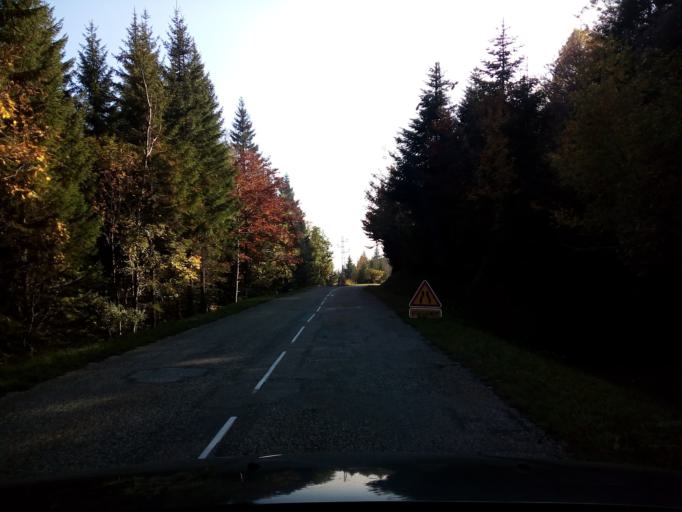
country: FR
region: Rhone-Alpes
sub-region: Departement de l'Isere
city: Bernin
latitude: 45.3009
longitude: 5.8407
